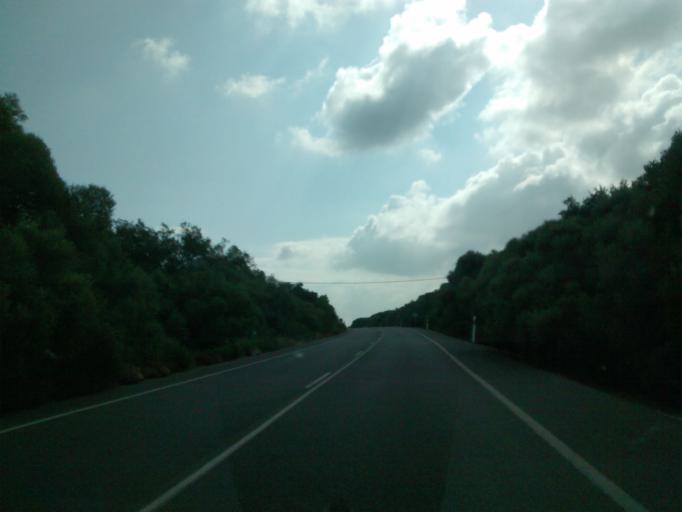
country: ES
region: Andalusia
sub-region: Provincia de Cadiz
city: Vejer de la Frontera
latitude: 36.2486
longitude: -5.9190
